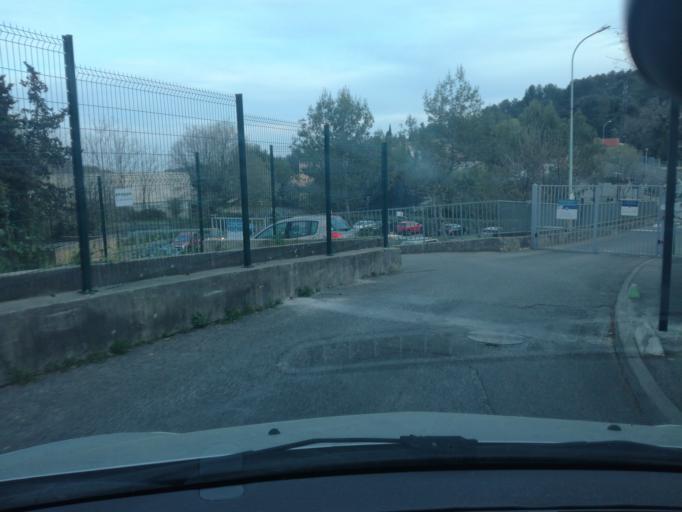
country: FR
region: Provence-Alpes-Cote d'Azur
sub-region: Departement des Alpes-Maritimes
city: Grasse
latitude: 43.6381
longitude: 6.9111
